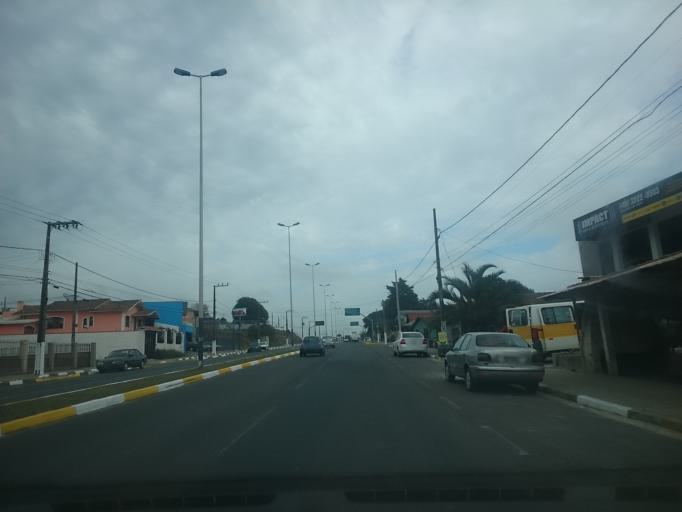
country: BR
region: Santa Catarina
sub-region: Lages
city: Lages
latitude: -27.8303
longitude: -50.3323
